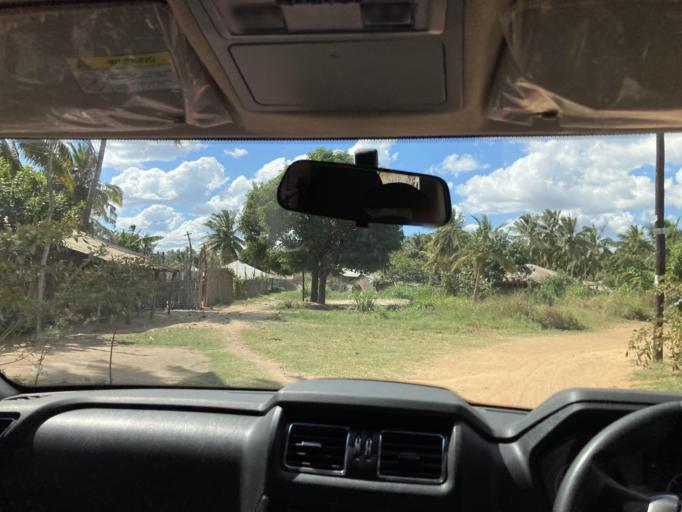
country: MZ
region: Cabo Delgado
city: Montepuez
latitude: -13.1360
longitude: 39.0031
